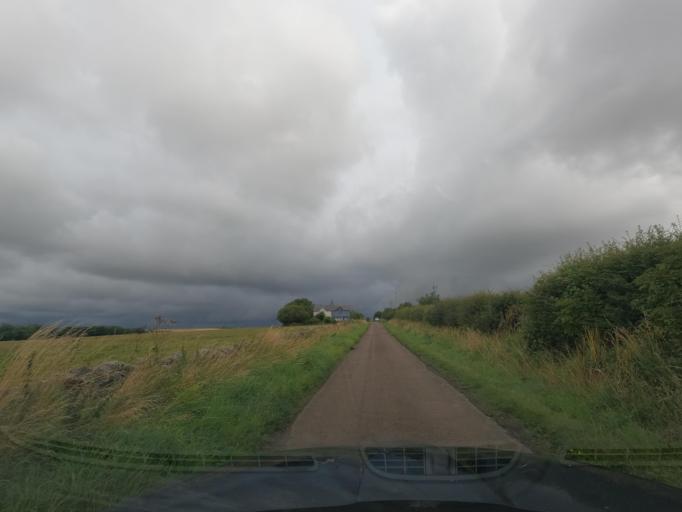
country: GB
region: England
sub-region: Northumberland
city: Ancroft
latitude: 55.7279
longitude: -2.0268
